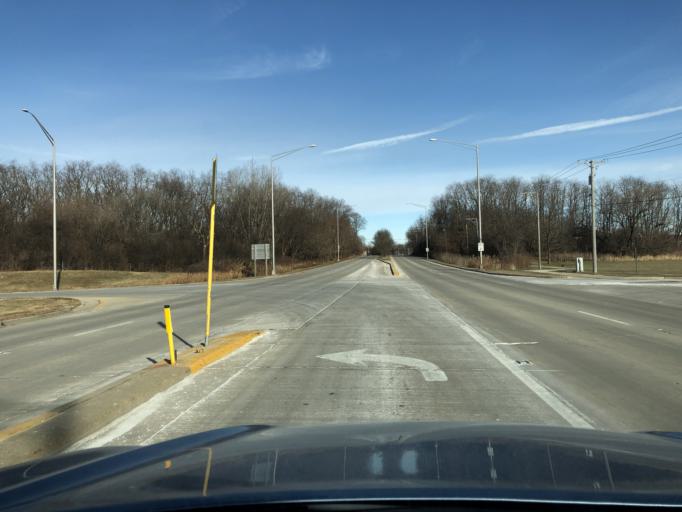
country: US
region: Illinois
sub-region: Lake County
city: Gurnee
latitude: 42.3588
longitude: -87.9339
